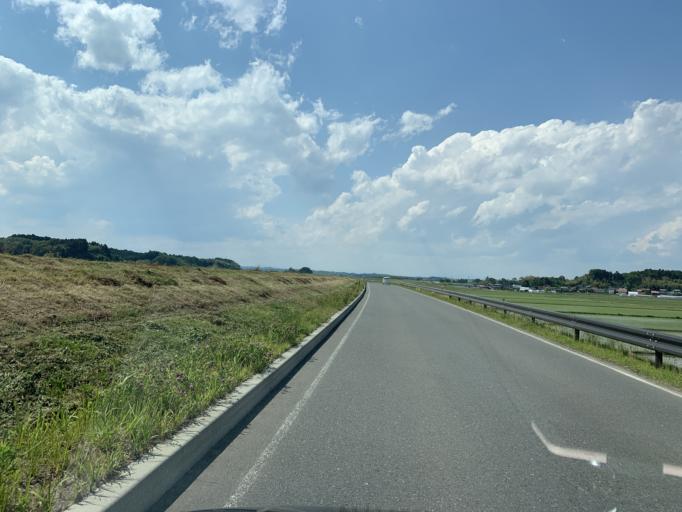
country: JP
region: Miyagi
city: Matsushima
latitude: 38.4317
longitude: 141.1230
